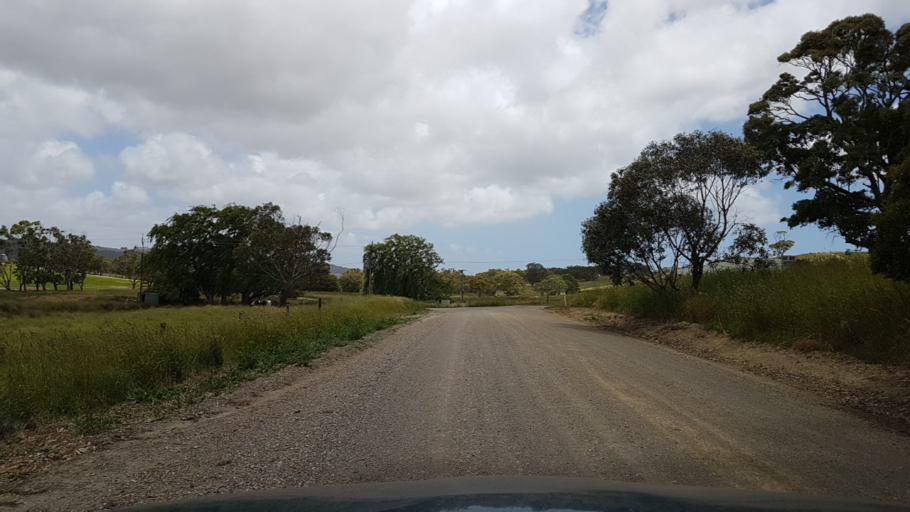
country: AU
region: South Australia
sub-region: Onkaparinga
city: Aldinga
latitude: -35.3698
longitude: 138.5195
